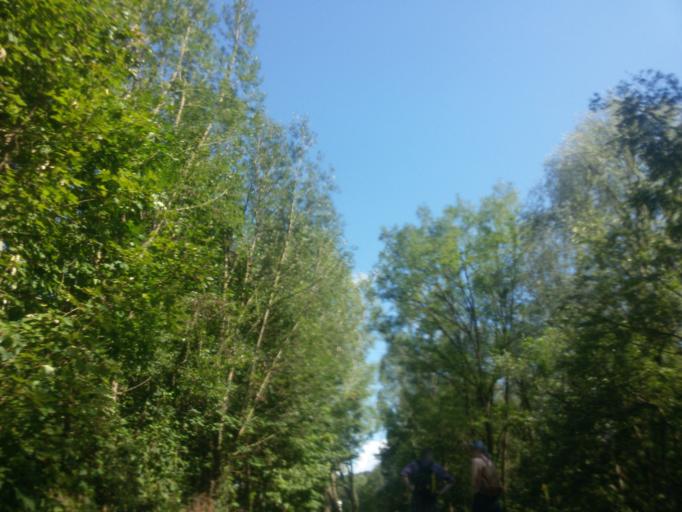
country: AT
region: Carinthia
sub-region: Villach Stadt
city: Villach
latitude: 46.6104
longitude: 13.8833
